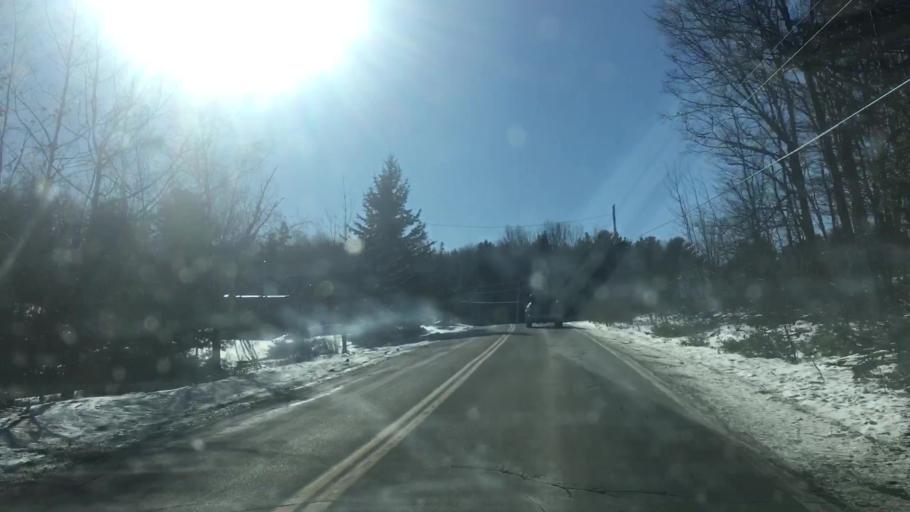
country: US
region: Maine
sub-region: Hancock County
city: Sedgwick
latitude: 44.3964
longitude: -68.6380
